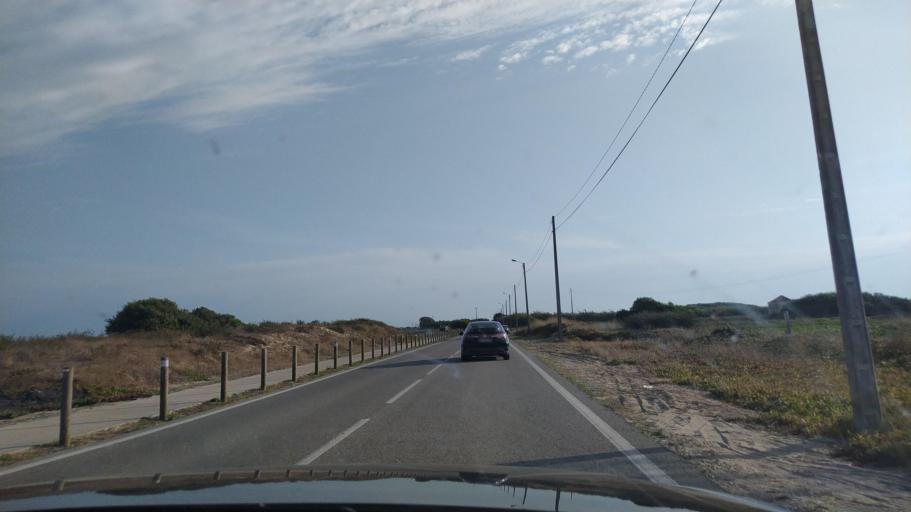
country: PT
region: Aveiro
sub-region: Ilhavo
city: Gafanha da Encarnacao
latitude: 40.5833
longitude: -8.7531
